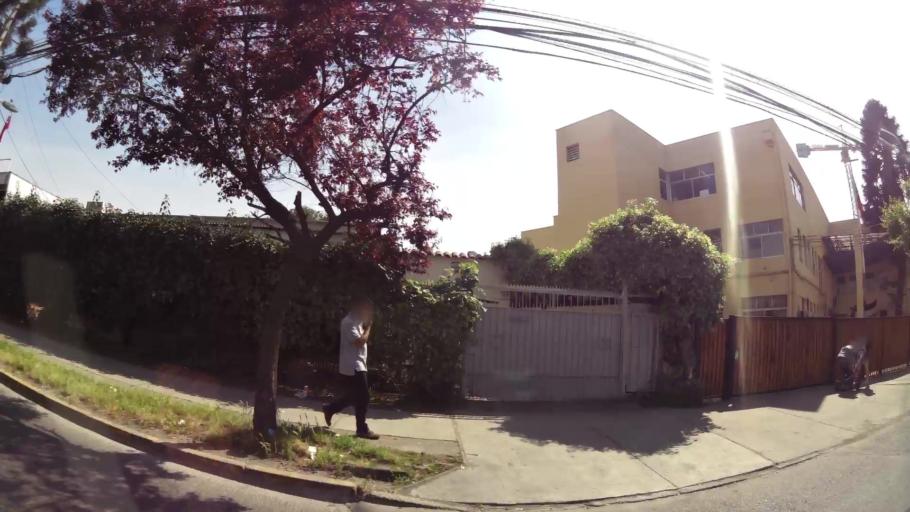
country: CL
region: Santiago Metropolitan
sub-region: Provincia de Santiago
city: Villa Presidente Frei, Nunoa, Santiago, Chile
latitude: -33.5226
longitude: -70.5823
